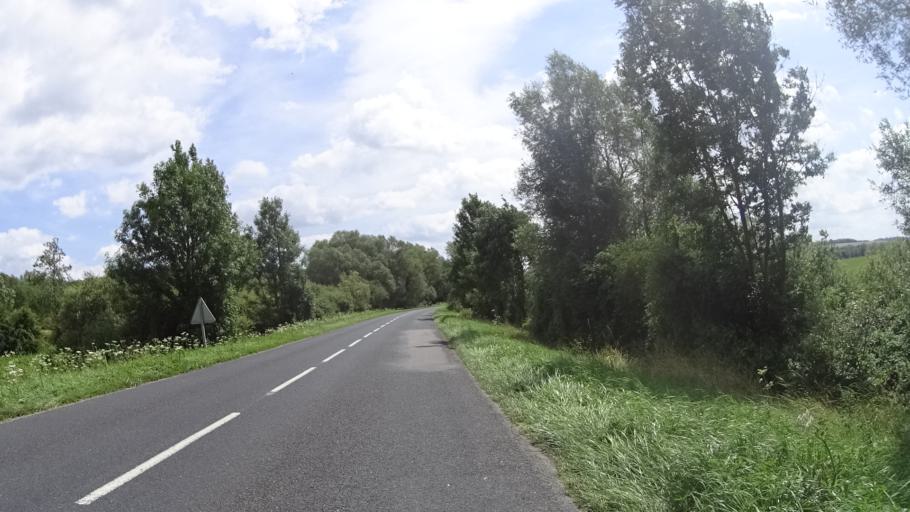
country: FR
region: Lorraine
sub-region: Departement de la Meuse
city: Euville
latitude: 48.7323
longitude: 5.6635
